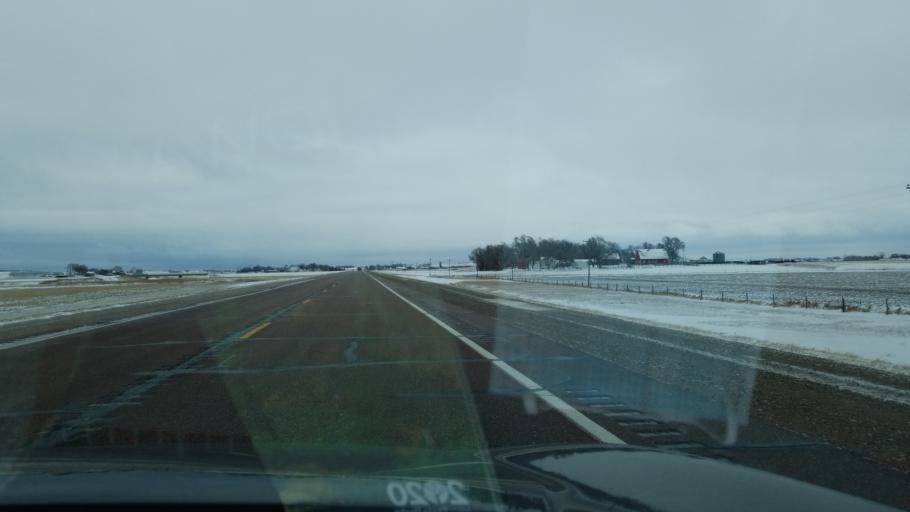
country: US
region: Iowa
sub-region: Plymouth County
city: Le Mars
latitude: 42.9175
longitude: -96.1749
